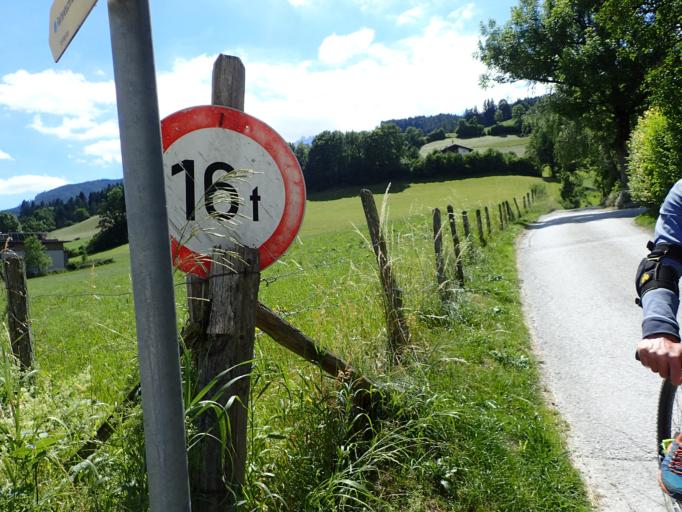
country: AT
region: Salzburg
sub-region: Politischer Bezirk Sankt Johann im Pongau
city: Werfen
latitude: 47.4718
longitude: 13.1908
